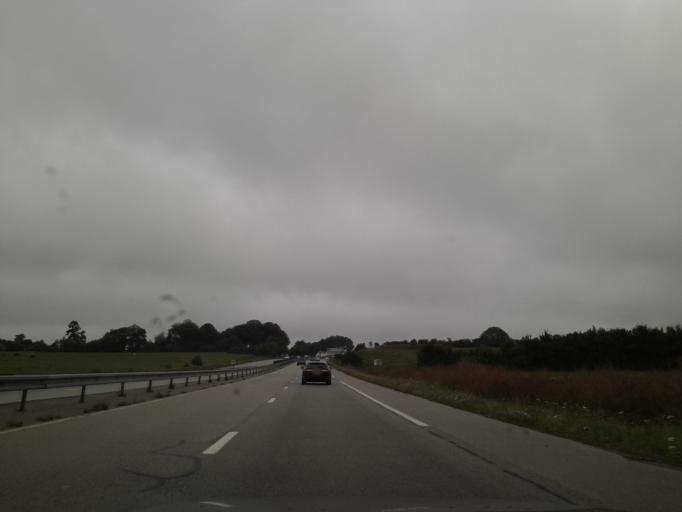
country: FR
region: Lower Normandy
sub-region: Departement de la Manche
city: Sainte-Mere-Eglise
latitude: 49.3916
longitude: -1.3045
